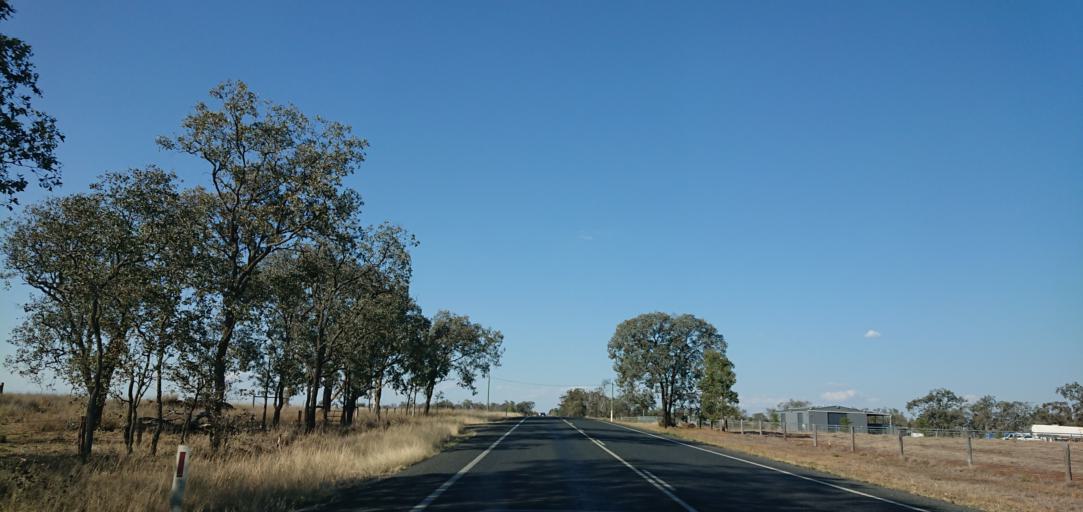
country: AU
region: Queensland
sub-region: Toowoomba
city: Westbrook
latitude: -27.6321
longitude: 151.7501
